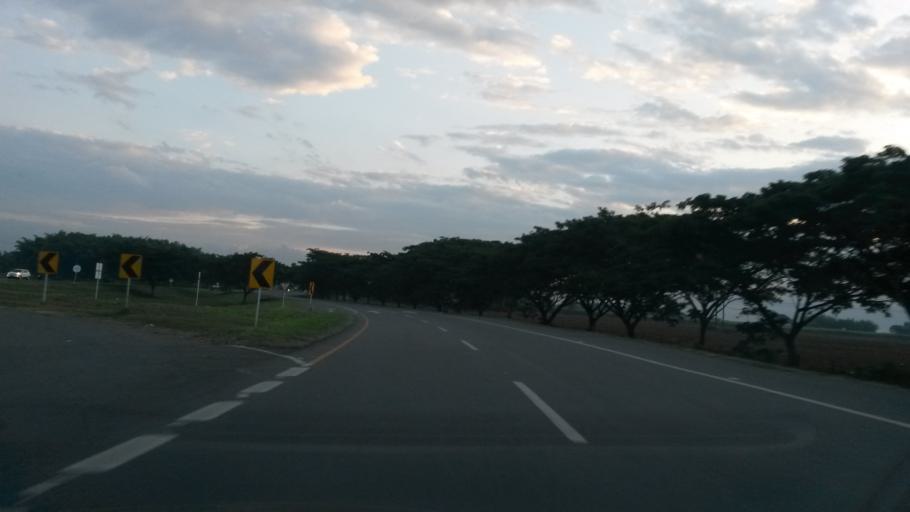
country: CO
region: Cauca
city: Santander de Quilichao
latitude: 3.0528
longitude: -76.4754
